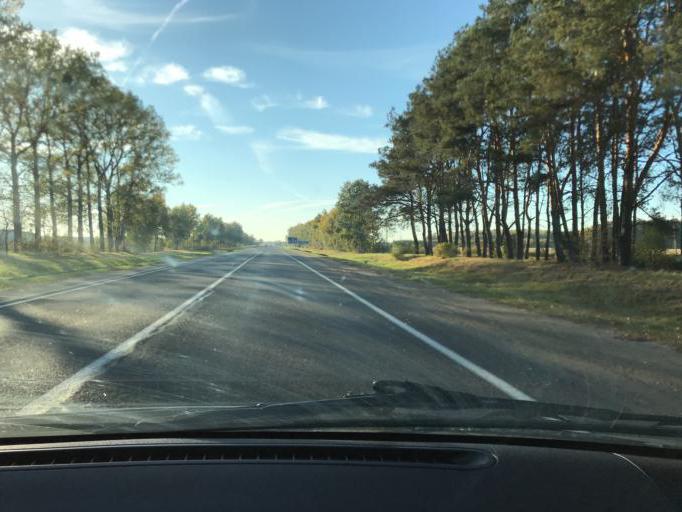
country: BY
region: Brest
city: Horad Kobryn
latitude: 52.2193
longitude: 24.4415
